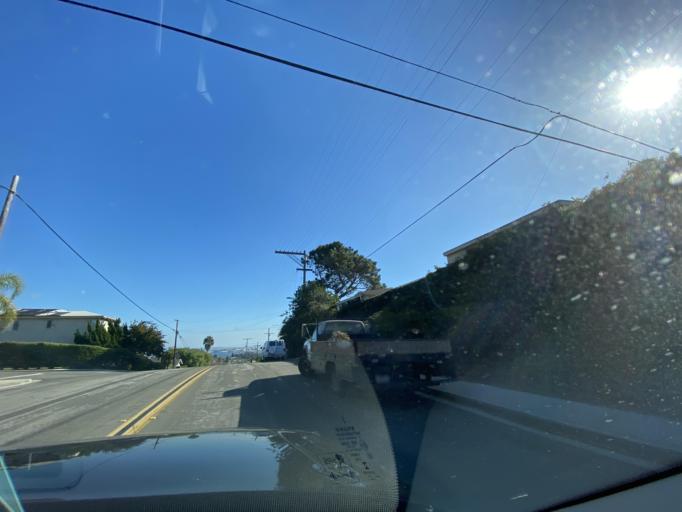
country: US
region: California
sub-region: San Diego County
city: Coronado
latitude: 32.7329
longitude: -117.2313
